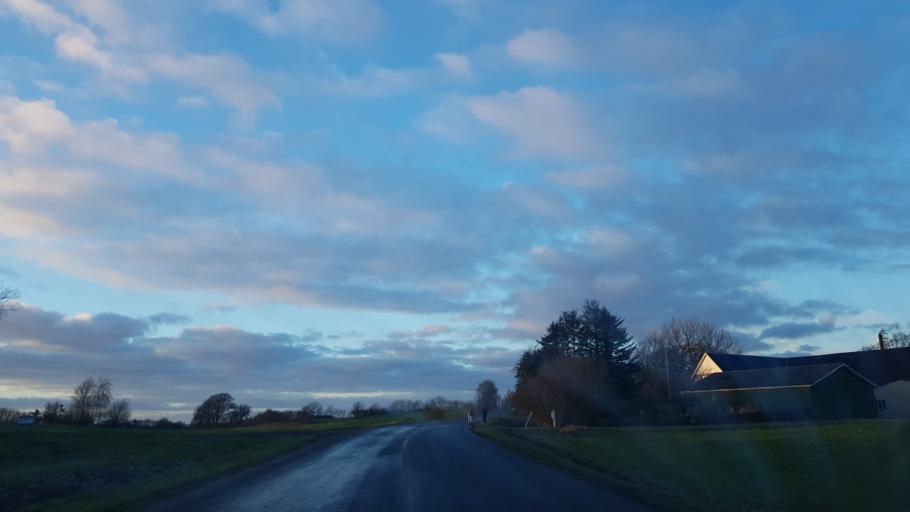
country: DK
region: South Denmark
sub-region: Kolding Kommune
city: Vamdrup
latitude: 55.3700
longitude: 9.3089
